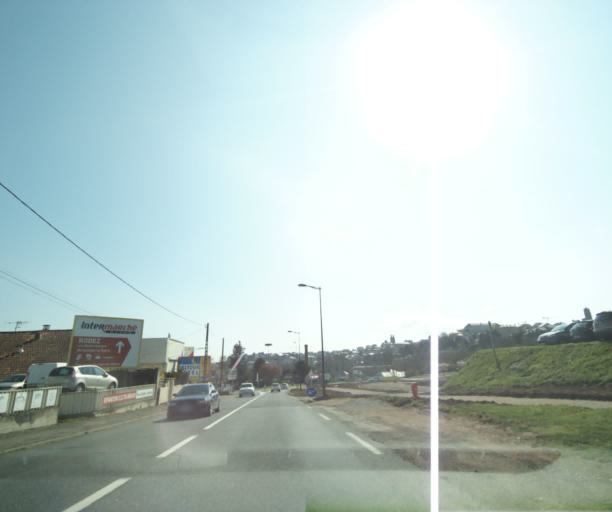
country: FR
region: Midi-Pyrenees
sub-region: Departement de l'Aveyron
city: Rodez
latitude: 44.3623
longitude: 2.5635
